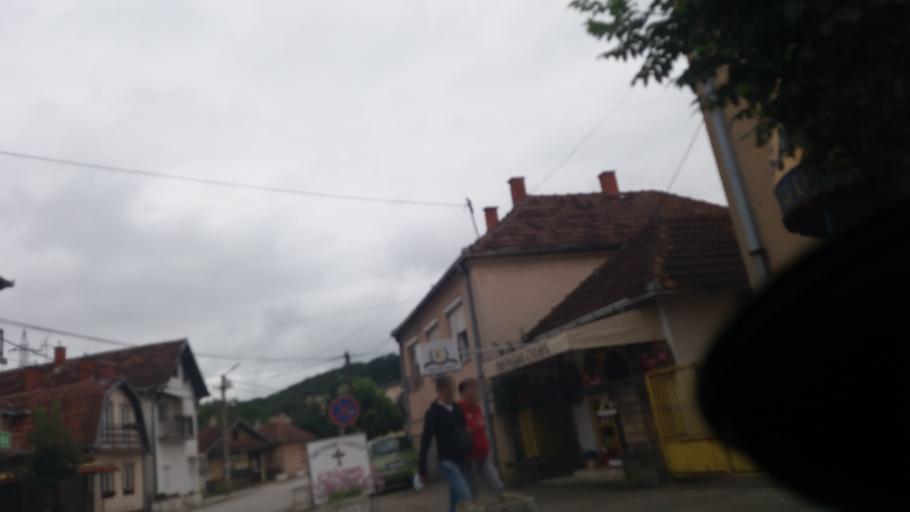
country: RS
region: Central Serbia
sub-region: Kolubarski Okrug
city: Ljig
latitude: 44.2270
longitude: 20.2380
